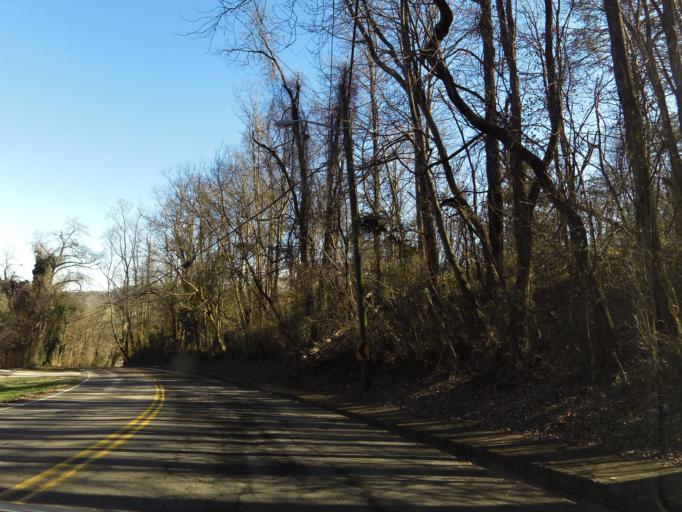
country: US
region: Tennessee
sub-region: Knox County
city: Knoxville
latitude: 35.9506
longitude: -83.9024
